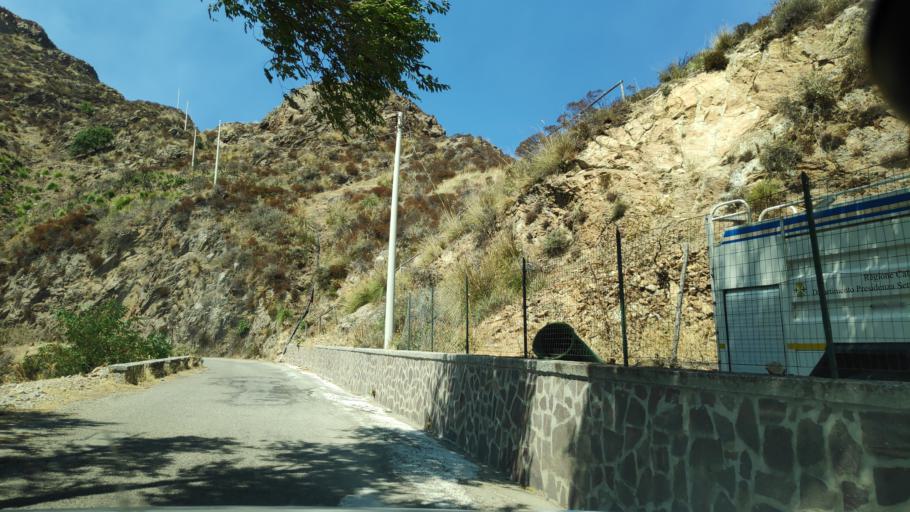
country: IT
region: Calabria
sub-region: Provincia di Reggio Calabria
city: Bova
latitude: 37.9992
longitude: 15.9304
